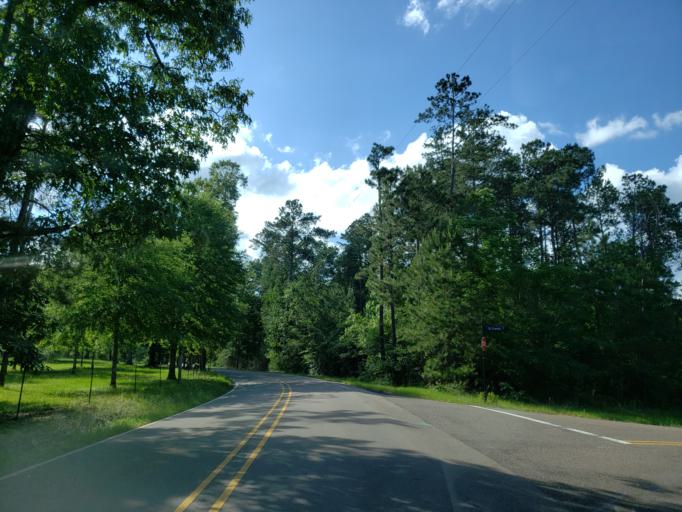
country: US
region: Mississippi
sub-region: Lamar County
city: Sumrall
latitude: 31.3540
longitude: -89.4763
